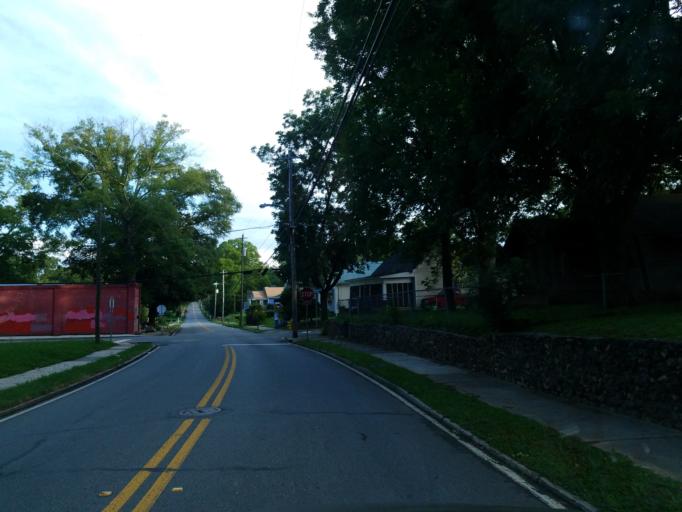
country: US
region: Georgia
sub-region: Bartow County
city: Cartersville
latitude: 34.1747
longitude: -84.7979
